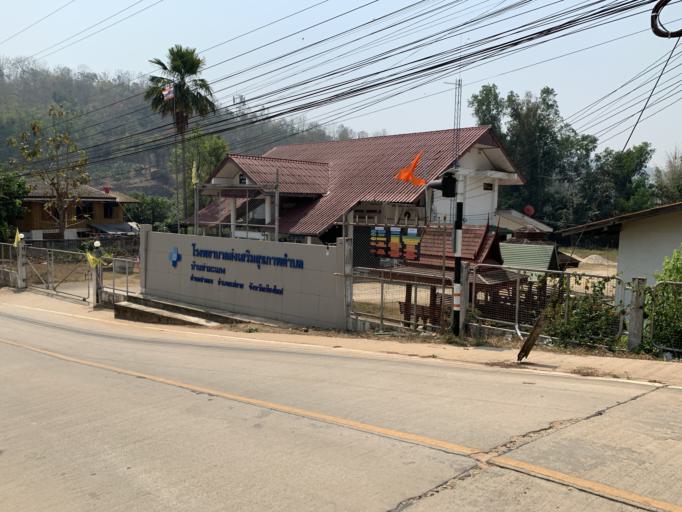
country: TH
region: Chiang Mai
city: Mae Ai
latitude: 20.0627
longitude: 99.4496
